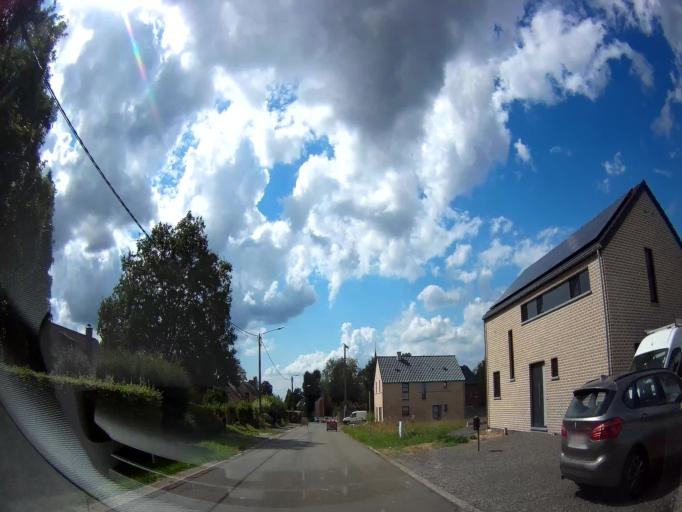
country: BE
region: Wallonia
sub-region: Province de Namur
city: Assesse
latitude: 50.3703
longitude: 5.0313
